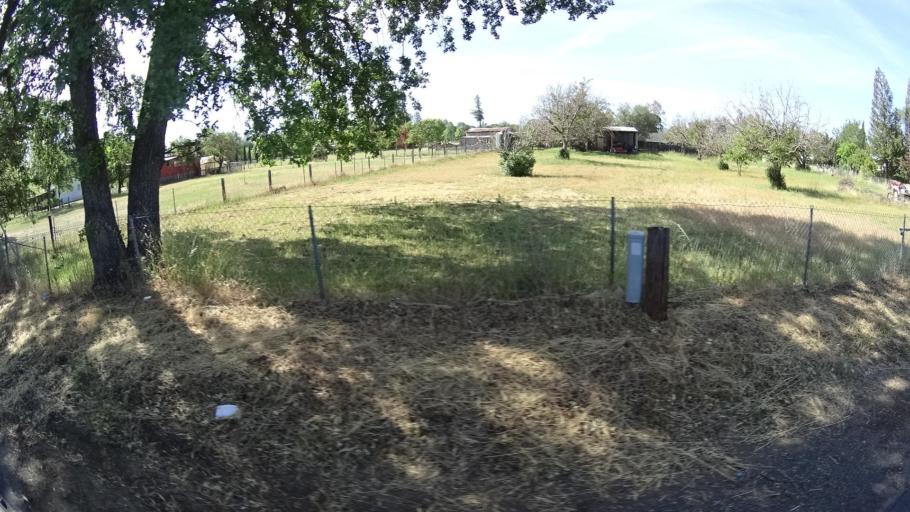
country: US
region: California
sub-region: Lake County
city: Kelseyville
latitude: 38.9714
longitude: -122.8621
